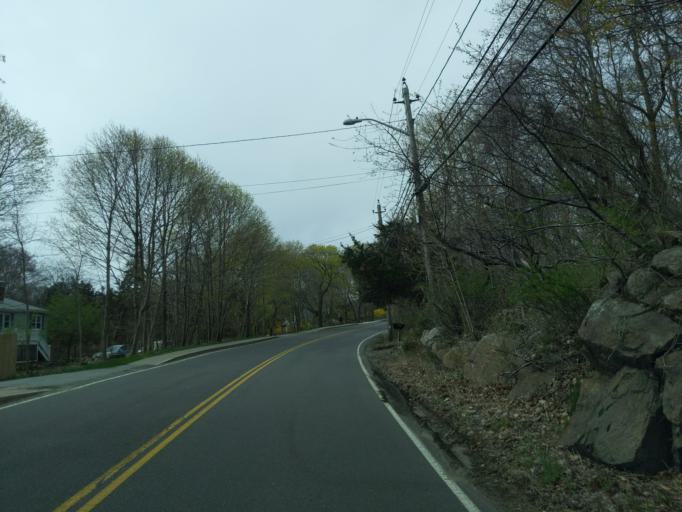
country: US
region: Massachusetts
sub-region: Essex County
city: Rockport
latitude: 42.6462
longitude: -70.5987
